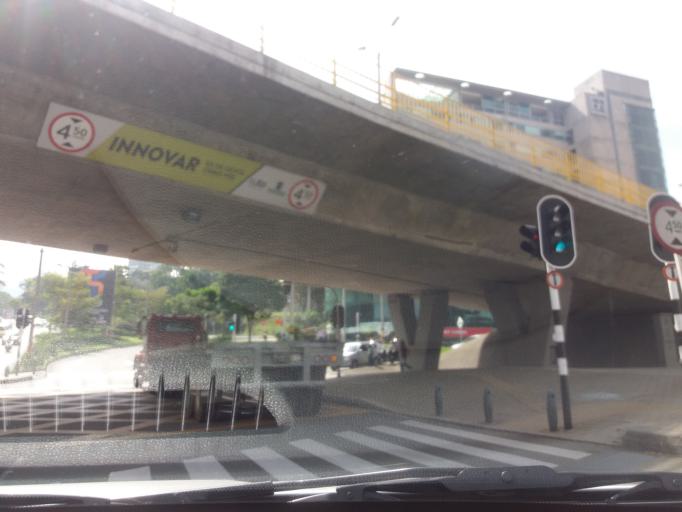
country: CO
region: Antioquia
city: Envigado
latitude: 6.1955
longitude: -75.5751
